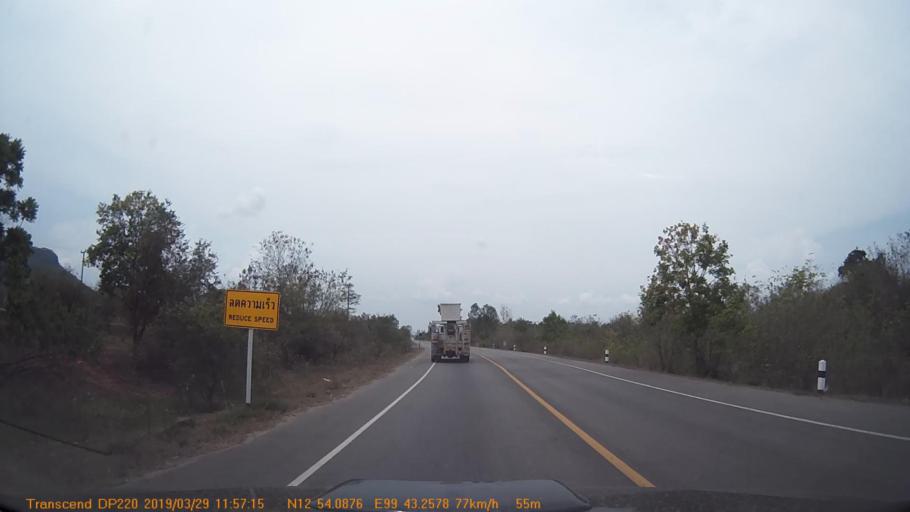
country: TH
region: Phetchaburi
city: Kaeng Krachan
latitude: 12.9012
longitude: 99.7208
